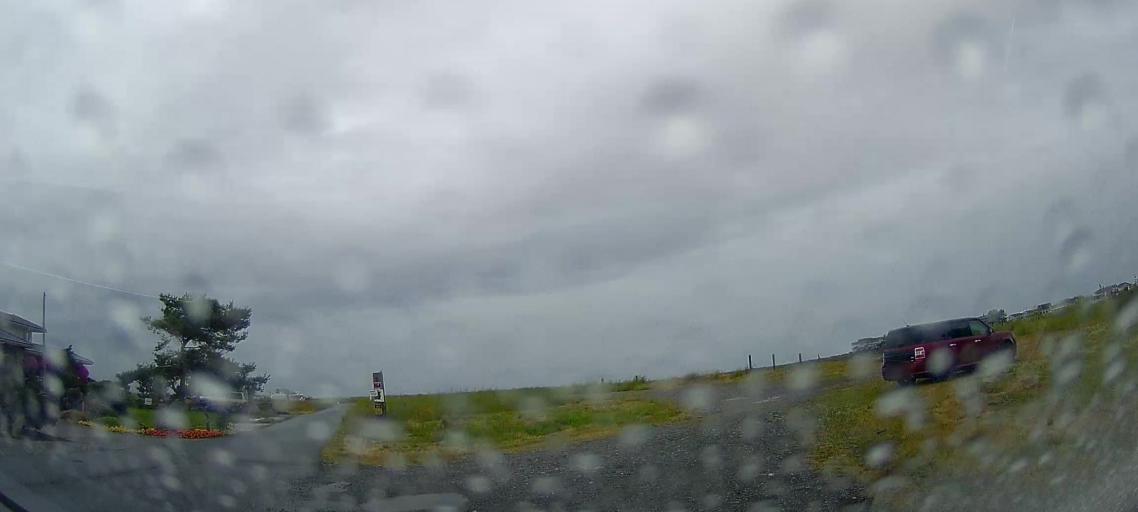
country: US
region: Washington
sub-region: Whatcom County
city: Marietta
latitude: 48.7872
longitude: -122.7046
